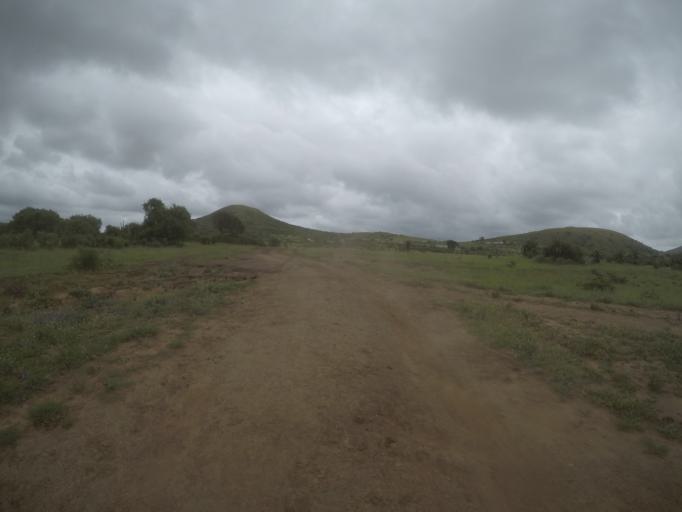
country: ZA
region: KwaZulu-Natal
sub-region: uThungulu District Municipality
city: Empangeni
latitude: -28.6057
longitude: 31.8652
